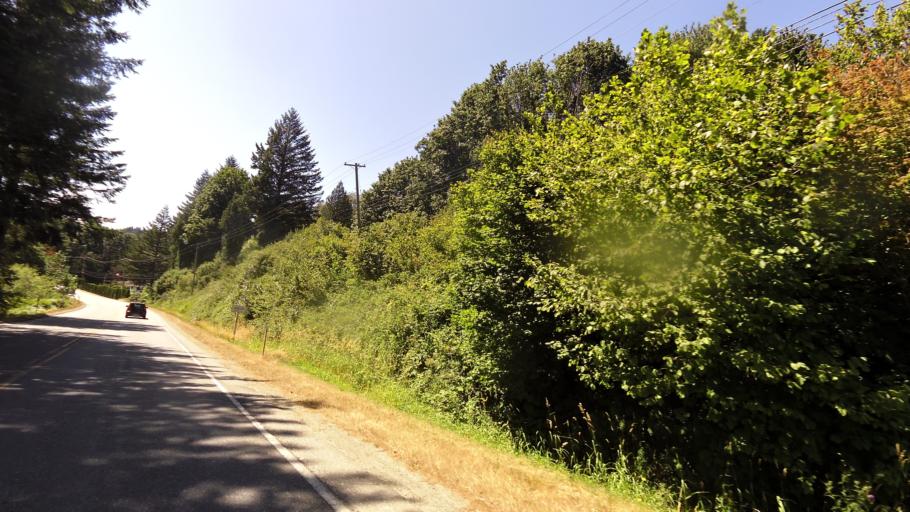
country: CA
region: British Columbia
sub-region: Fraser Valley Regional District
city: Chilliwack
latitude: 49.1932
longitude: -122.0671
